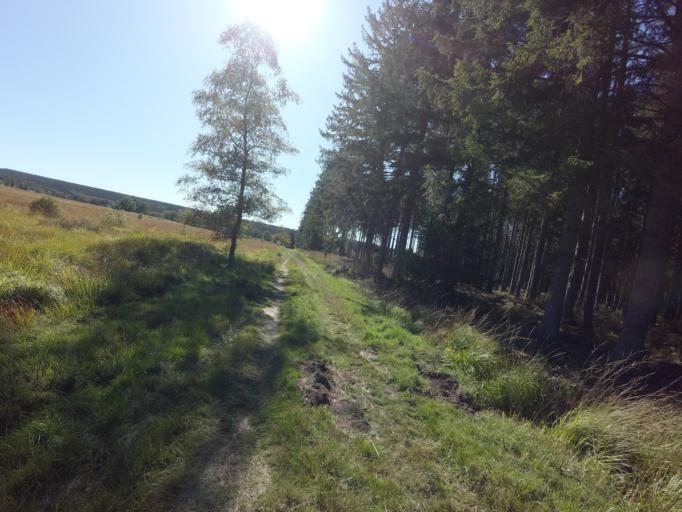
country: BE
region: Wallonia
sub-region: Province de Liege
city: Raeren
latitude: 50.5981
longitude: 6.1452
